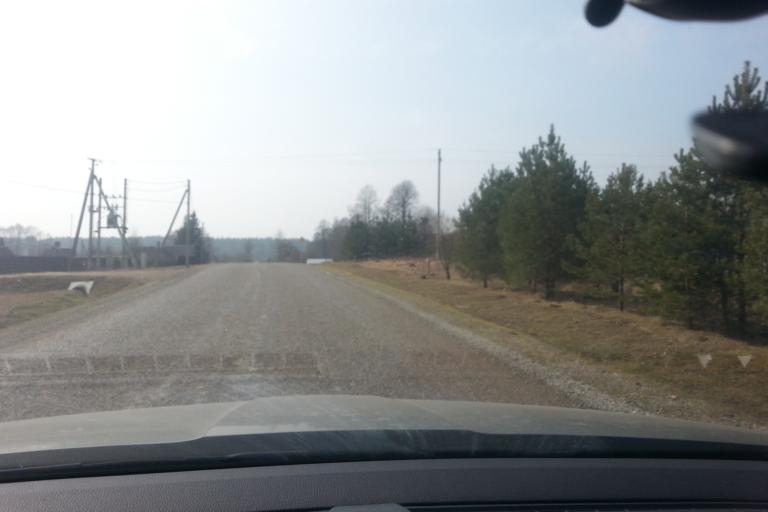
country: LT
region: Vilnius County
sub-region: Trakai
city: Rudiskes
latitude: 54.5185
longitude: 24.9406
